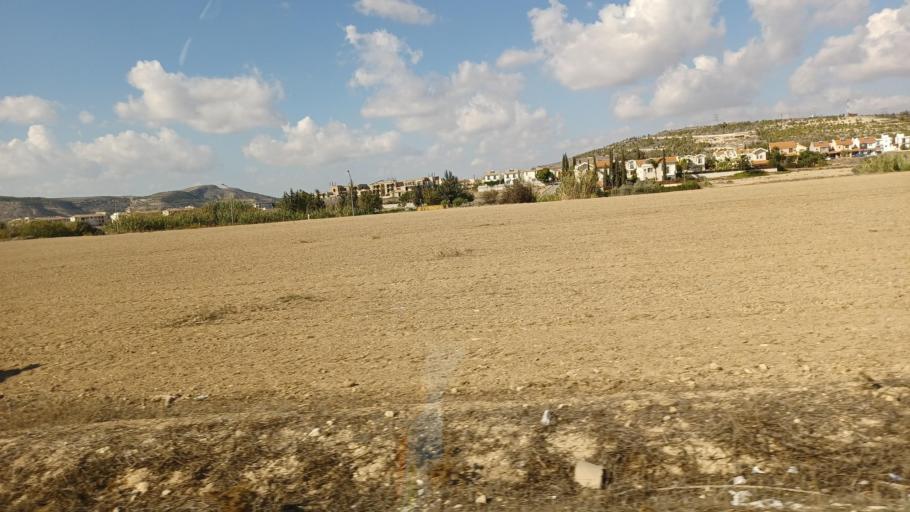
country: CY
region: Larnaka
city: Pyla
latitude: 34.9957
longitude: 33.6845
